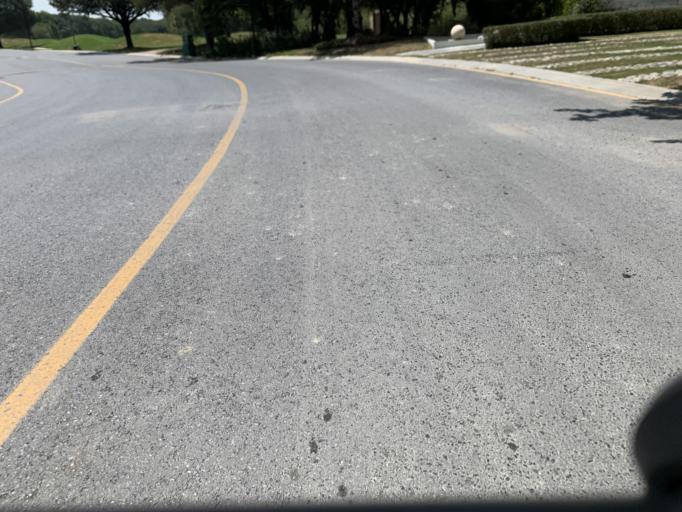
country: MX
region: Nuevo Leon
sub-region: Juarez
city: Bosques de San Pedro
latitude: 25.5131
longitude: -100.1915
